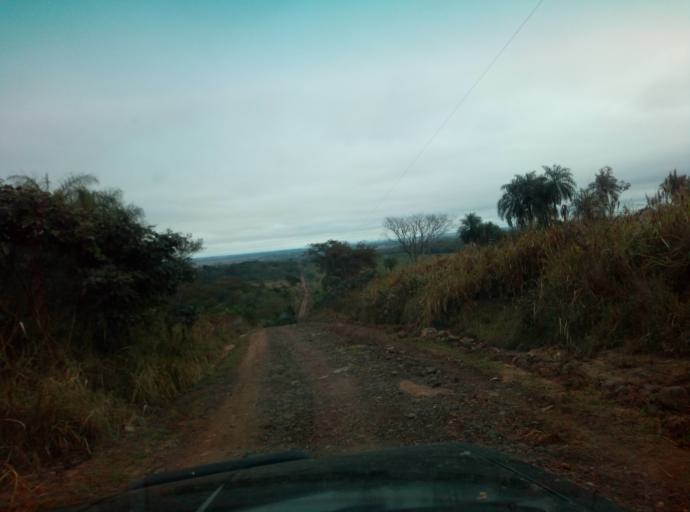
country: PY
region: Caaguazu
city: Carayao
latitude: -25.1904
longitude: -56.3668
